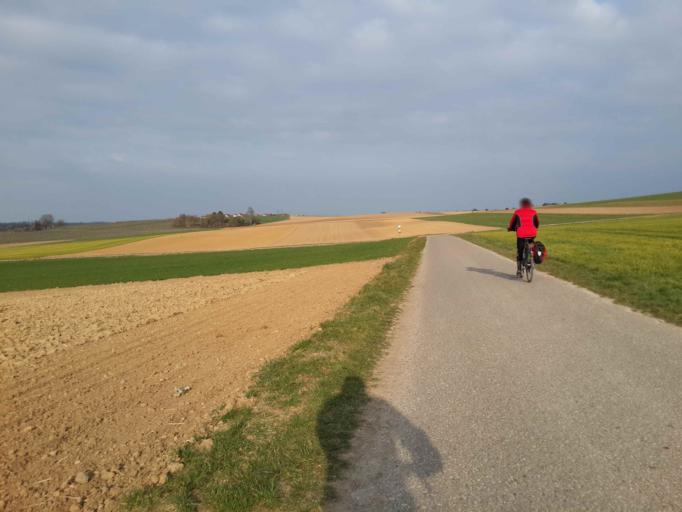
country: DE
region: Baden-Wuerttemberg
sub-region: Regierungsbezirk Stuttgart
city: Leingarten
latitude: 49.1364
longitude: 9.0917
